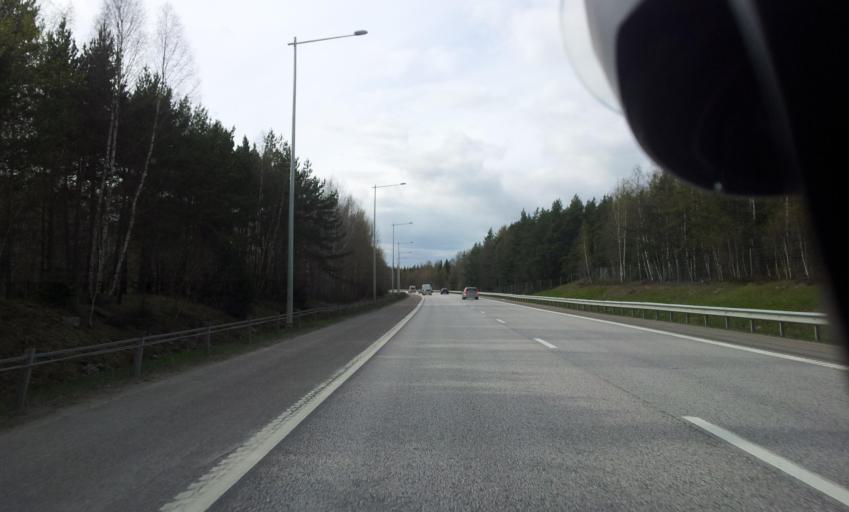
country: SE
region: Stockholm
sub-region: Upplands-Bro Kommun
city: Bro
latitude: 59.5210
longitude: 17.6634
